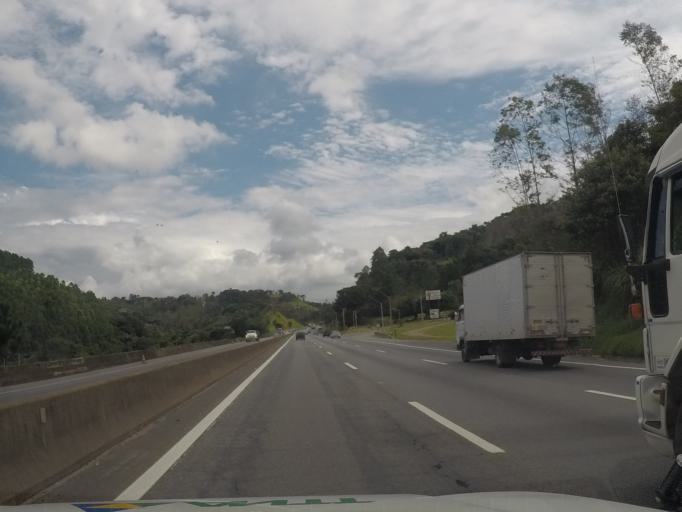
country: BR
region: Sao Paulo
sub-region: Mairipora
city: Mairipora
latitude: -23.2246
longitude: -46.5973
